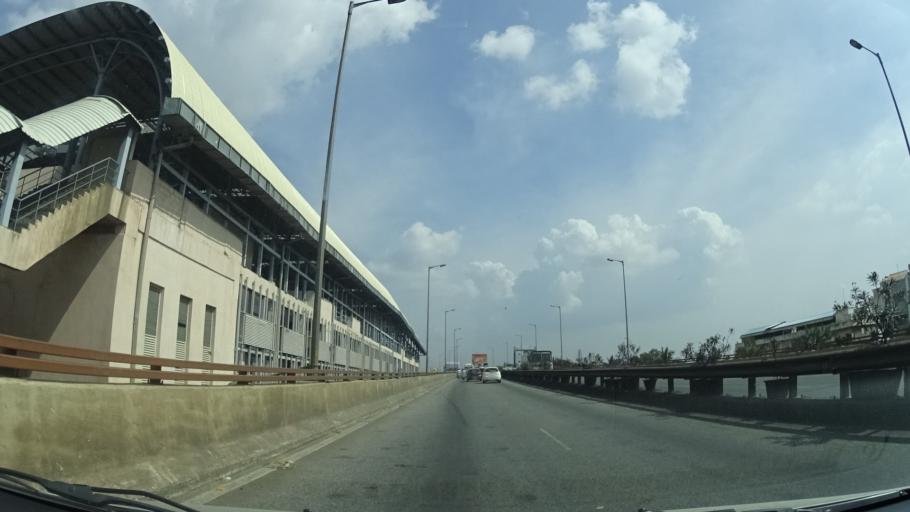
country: IN
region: Karnataka
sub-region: Bangalore Urban
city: Bangalore
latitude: 13.0365
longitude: 77.5247
